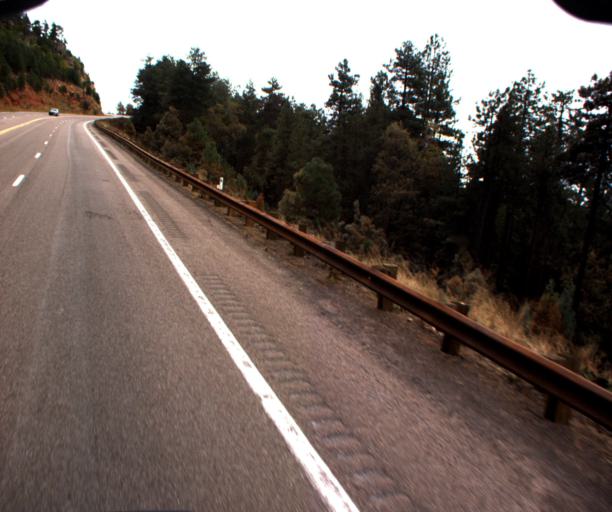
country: US
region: Arizona
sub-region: Gila County
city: Star Valley
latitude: 34.3017
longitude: -110.9110
